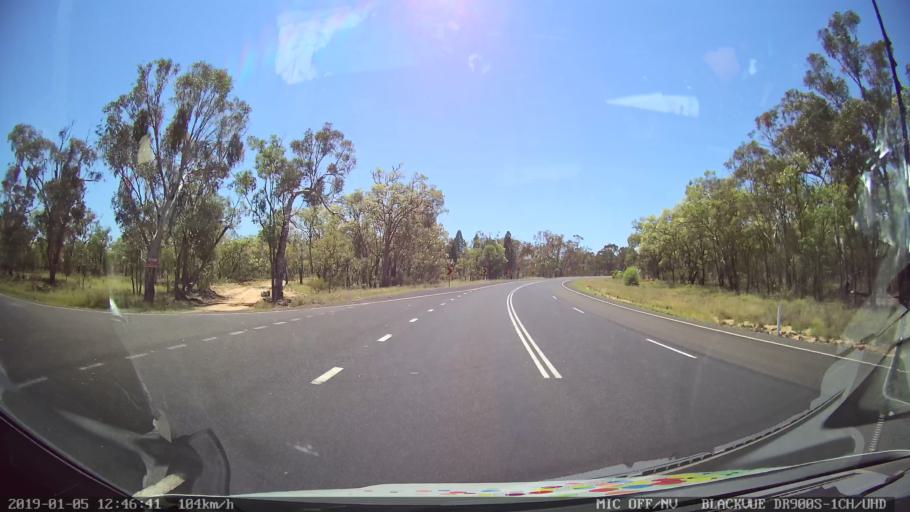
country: AU
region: New South Wales
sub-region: Warrumbungle Shire
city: Coonabarabran
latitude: -31.1154
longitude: 149.5659
